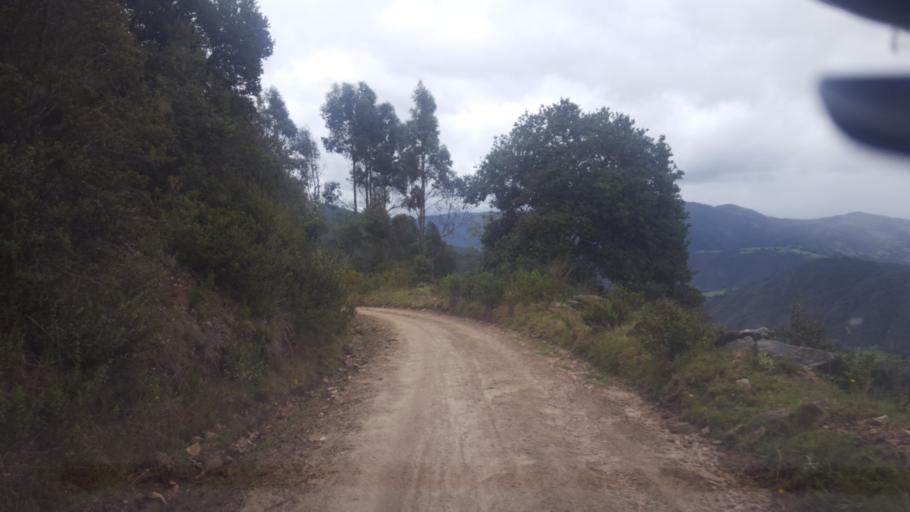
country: CO
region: Boyaca
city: Belen
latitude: 6.0301
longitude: -72.8826
